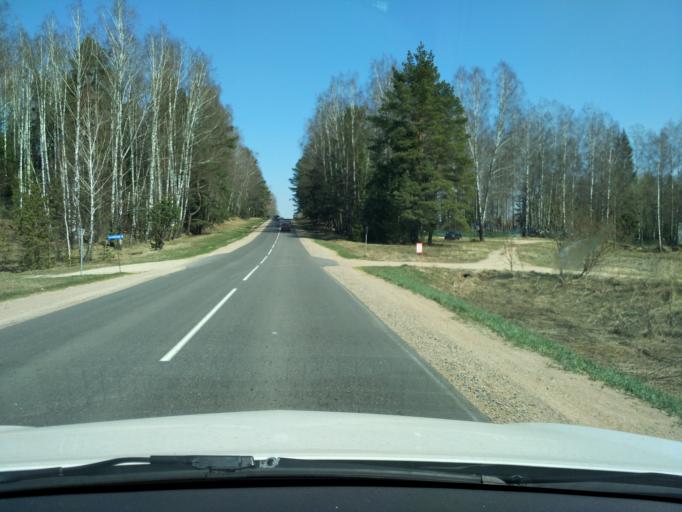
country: BY
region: Minsk
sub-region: Smalyavitski Rayon
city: Usjazh
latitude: 53.9984
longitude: 27.9916
